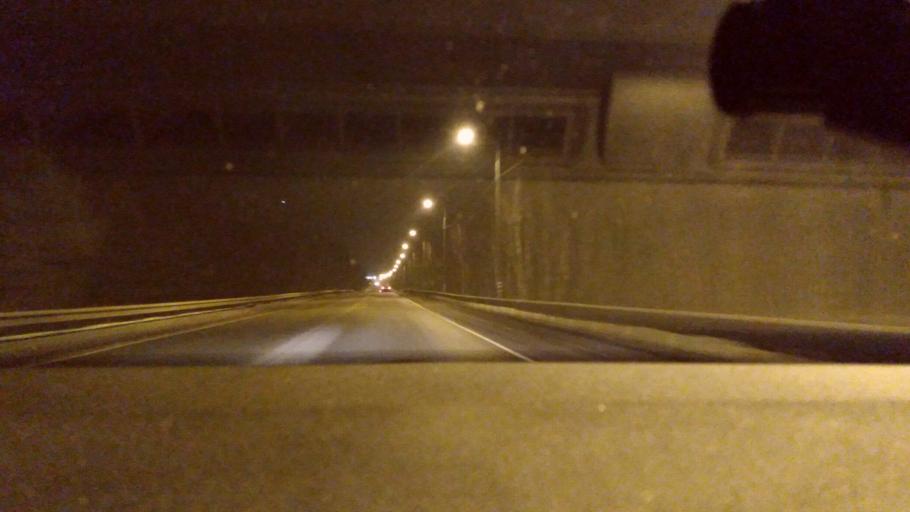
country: RU
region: Moskovskaya
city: Il'inskiy Pogost
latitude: 55.4875
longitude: 38.9050
